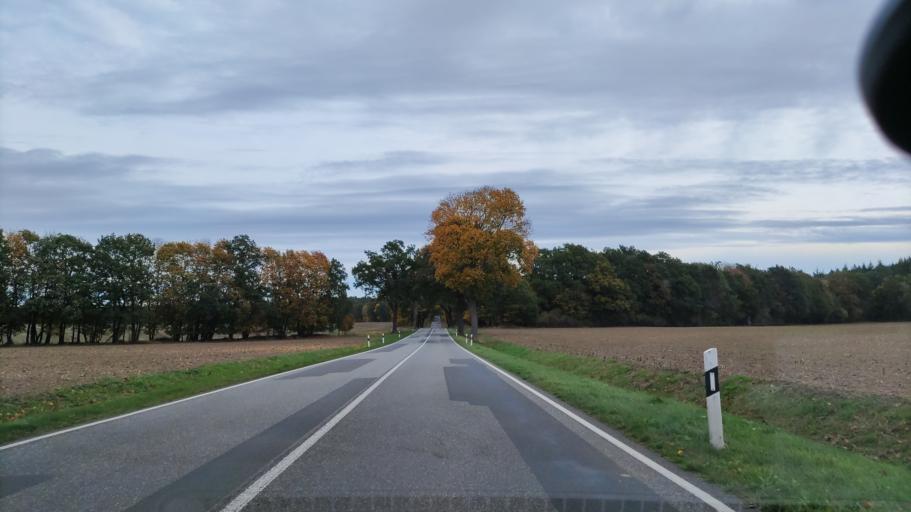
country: DE
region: Mecklenburg-Vorpommern
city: Lubtheen
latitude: 53.3961
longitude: 10.9898
